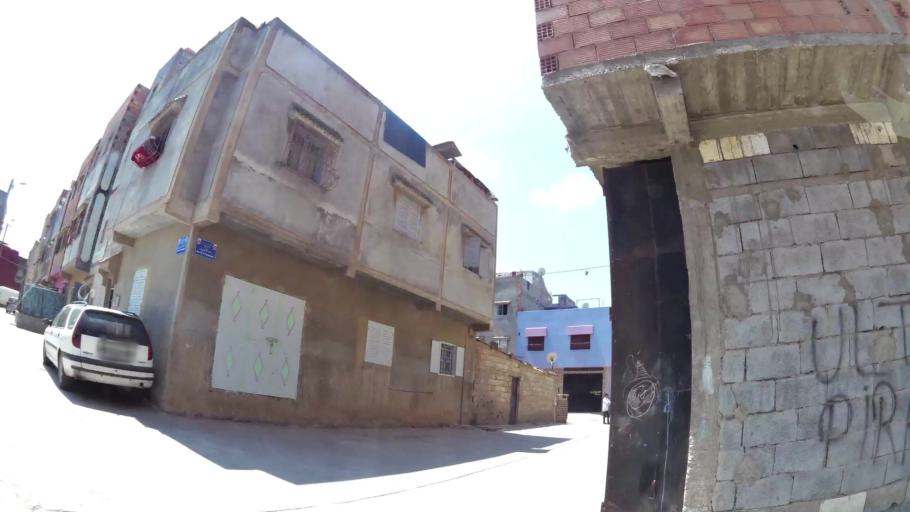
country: MA
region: Rabat-Sale-Zemmour-Zaer
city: Sale
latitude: 34.0702
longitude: -6.7838
